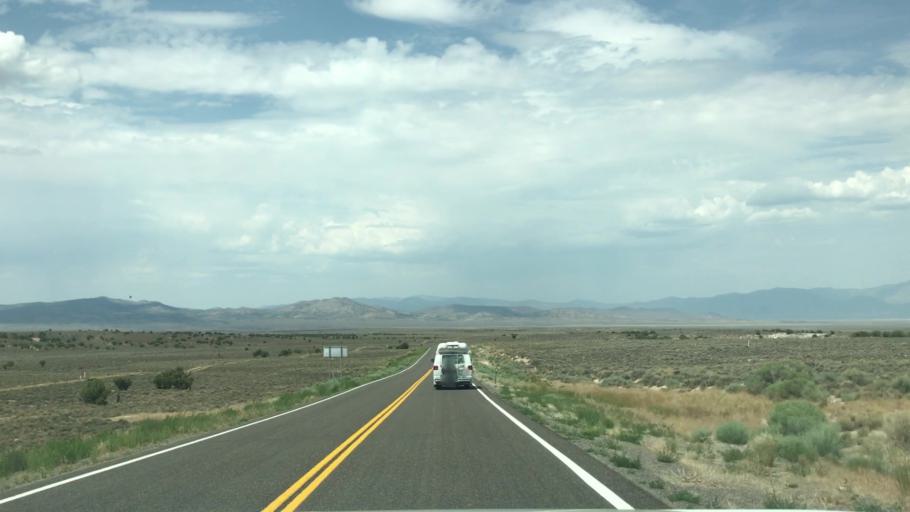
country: US
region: Nevada
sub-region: Eureka County
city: Eureka
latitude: 39.3946
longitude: -115.5277
